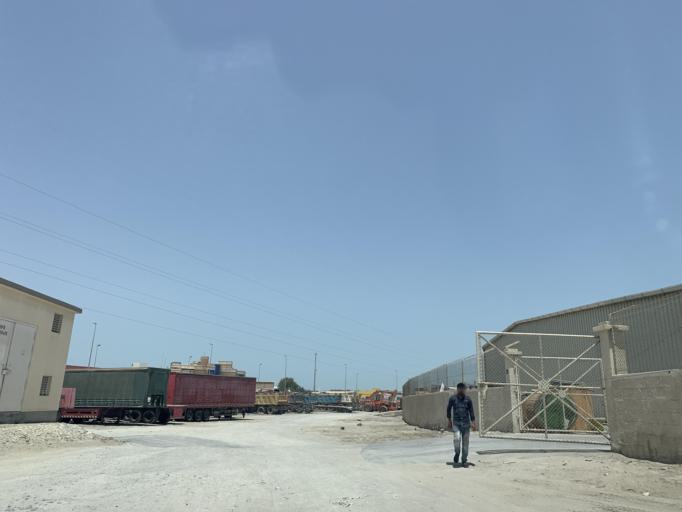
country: BH
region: Northern
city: Sitrah
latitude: 26.1761
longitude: 50.6062
